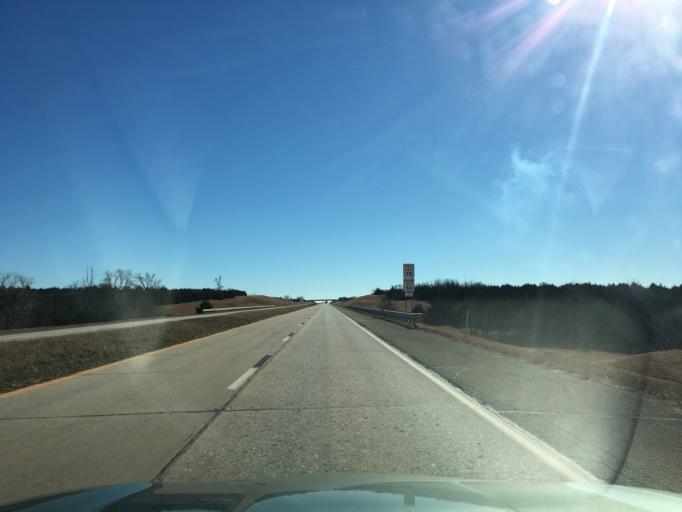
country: US
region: Oklahoma
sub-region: Pawnee County
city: Pawnee
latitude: 36.2876
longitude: -96.9831
